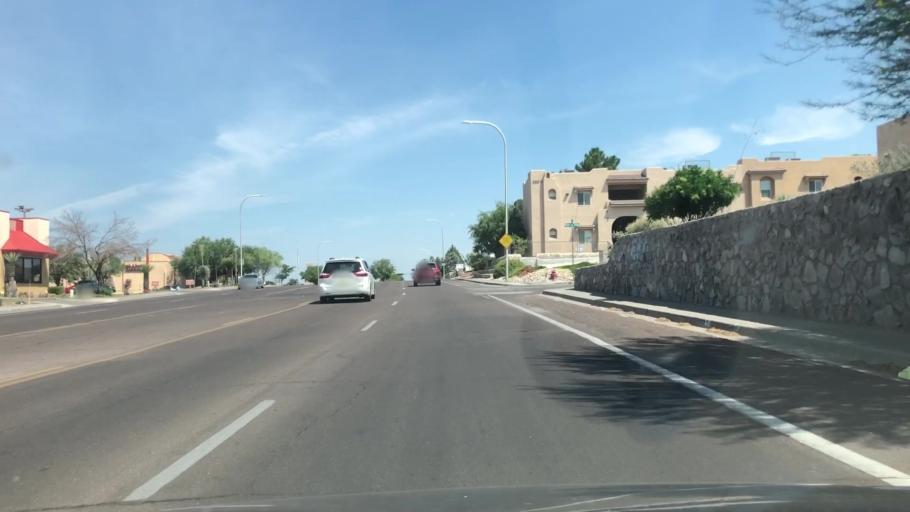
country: US
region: New Mexico
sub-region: Dona Ana County
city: University Park
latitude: 32.3077
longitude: -106.7391
